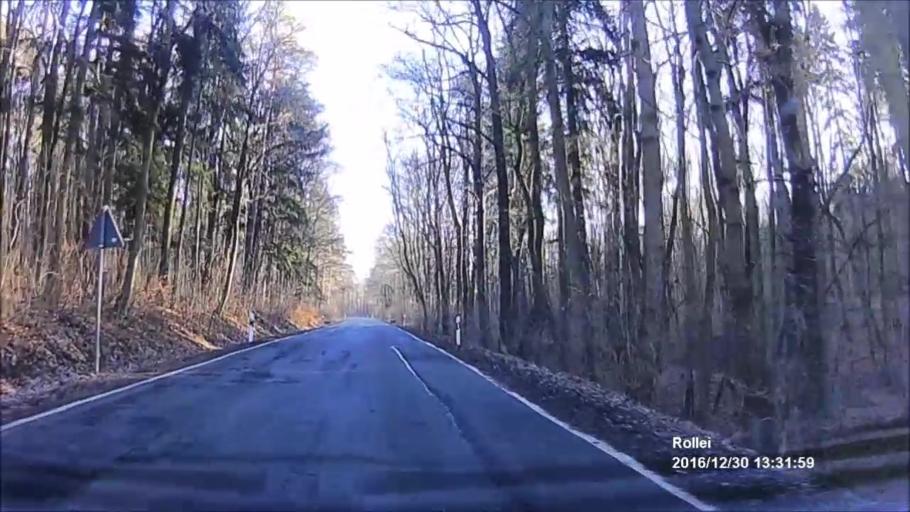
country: DE
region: Thuringia
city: Klettbach
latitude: 50.9316
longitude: 11.1037
